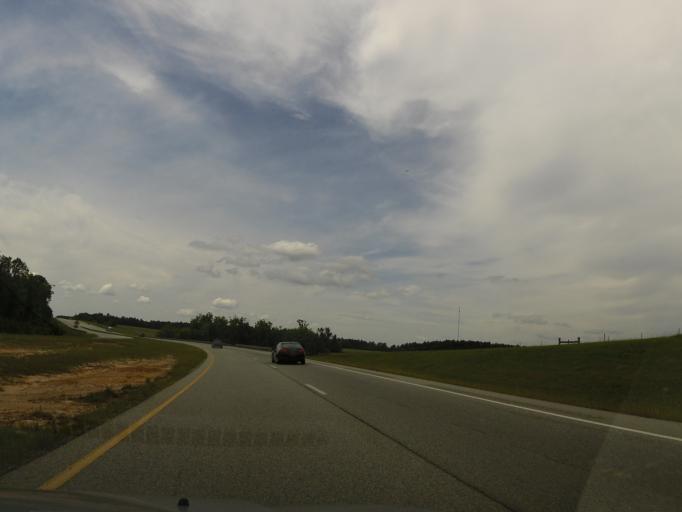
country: US
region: Georgia
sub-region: Emanuel County
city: Swainsboro
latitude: 32.5311
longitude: -82.3027
